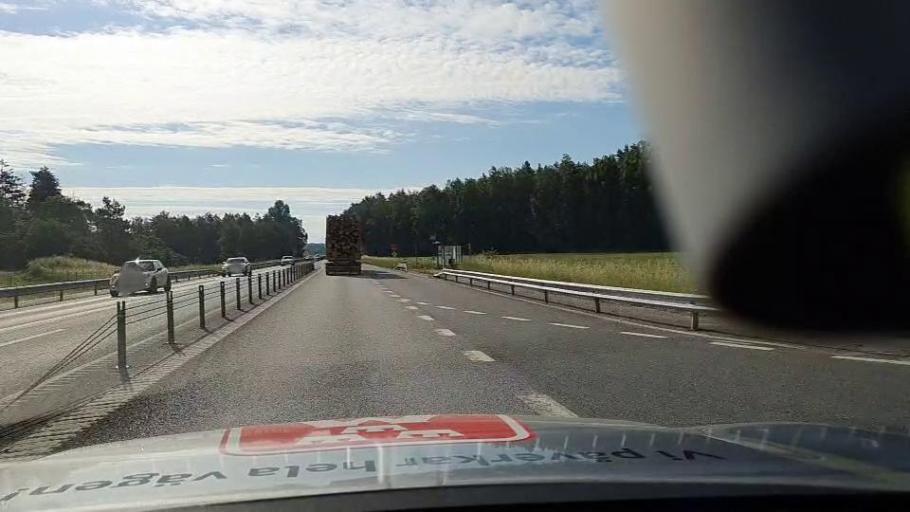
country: SE
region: Skane
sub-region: Kristianstads Kommun
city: Fjalkinge
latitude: 56.0412
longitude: 14.3291
